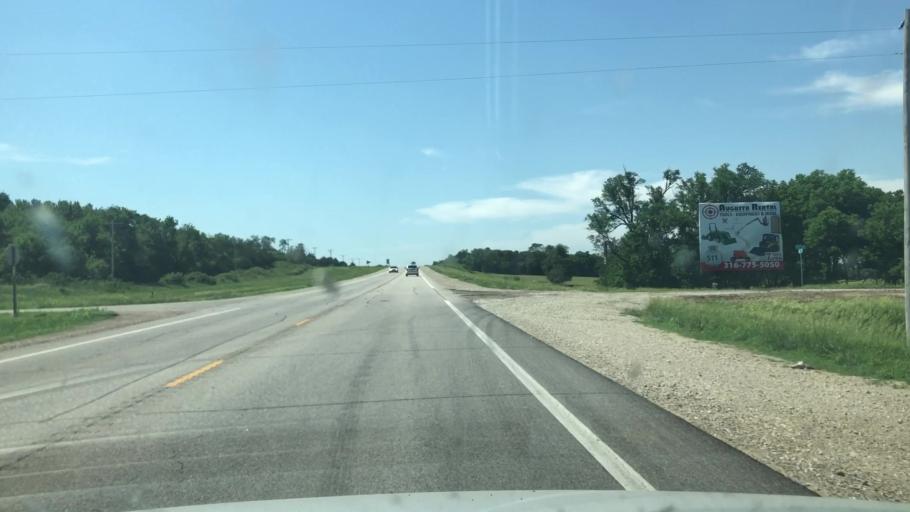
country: US
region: Kansas
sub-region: Cowley County
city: Winfield
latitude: 37.3759
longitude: -97.0070
